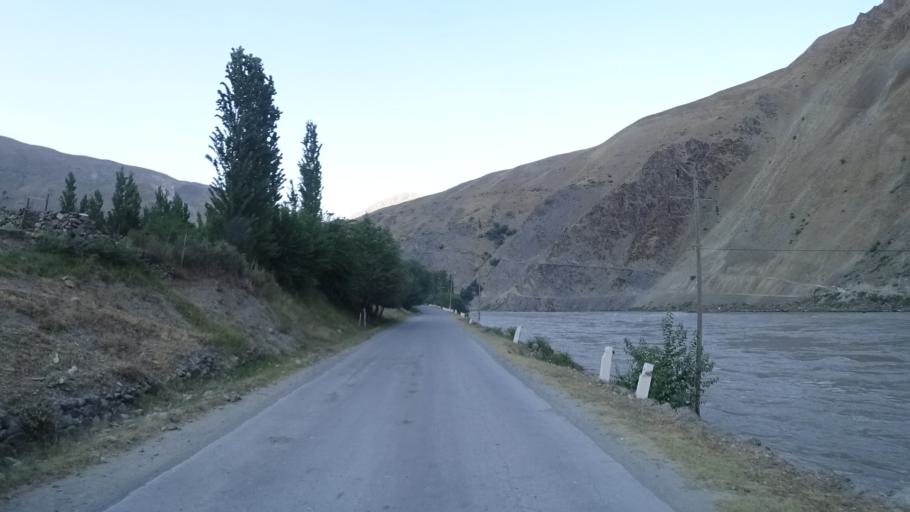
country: TJ
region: Gorno-Badakhshan
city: Qalaikhumb
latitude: 38.4431
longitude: 70.7628
